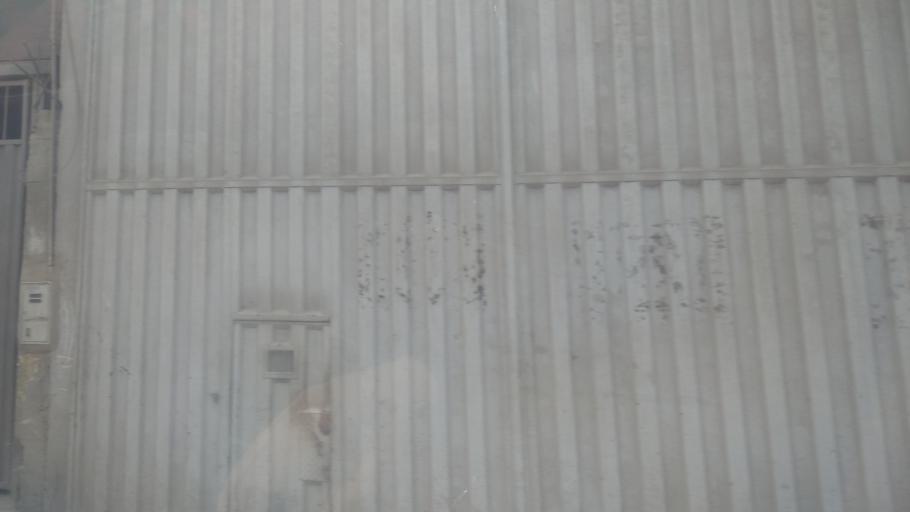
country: PE
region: Lima
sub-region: Lima
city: Independencia
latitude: -11.9783
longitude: -77.0083
